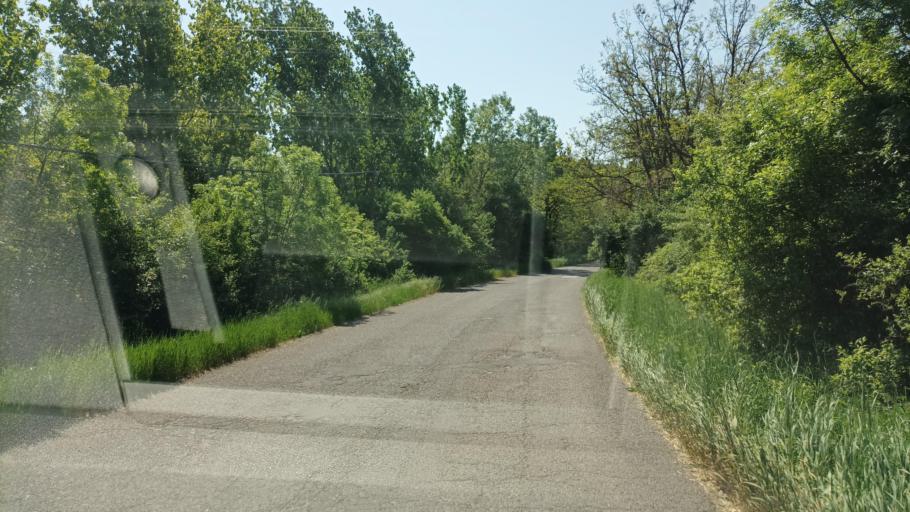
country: HU
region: Pest
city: Uri
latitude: 47.3912
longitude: 19.4991
